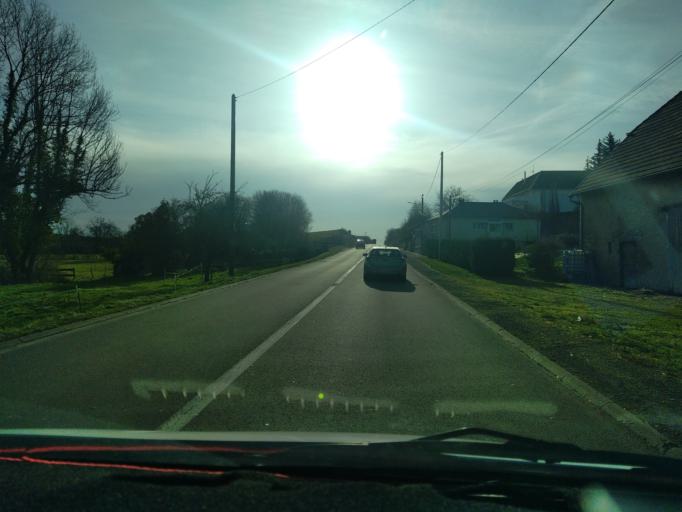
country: FR
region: Franche-Comte
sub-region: Departement de la Haute-Saone
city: Gray
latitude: 47.3890
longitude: 5.6543
